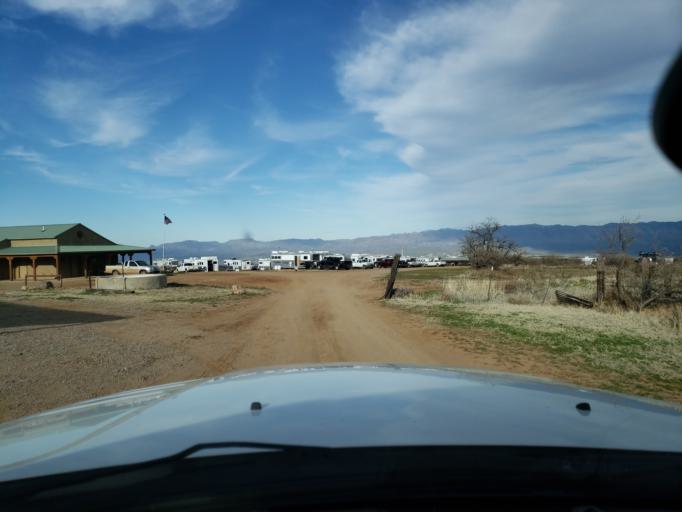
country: US
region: Arizona
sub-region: Pinal County
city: San Manuel
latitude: 32.5486
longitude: -110.7043
